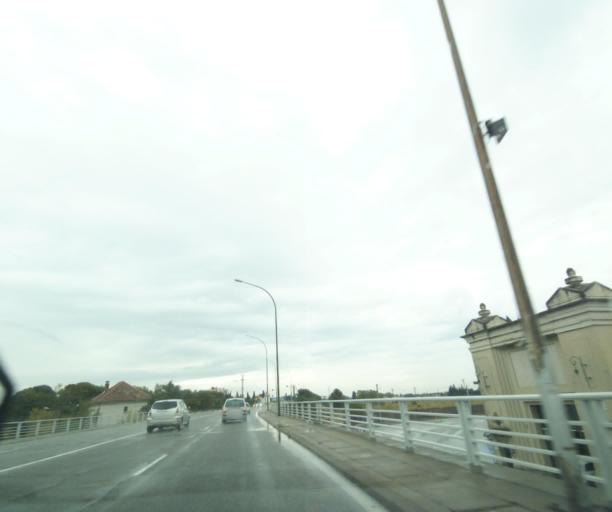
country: FR
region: Languedoc-Roussillon
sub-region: Departement du Gard
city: Rodilhan
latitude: 43.8463
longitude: 4.3962
